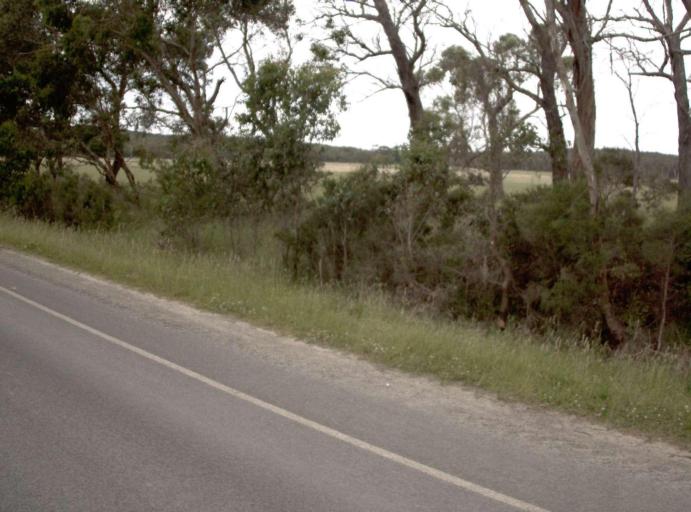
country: AU
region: Victoria
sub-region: Cardinia
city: Koo-Wee-Rup
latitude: -38.3309
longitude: 145.5982
